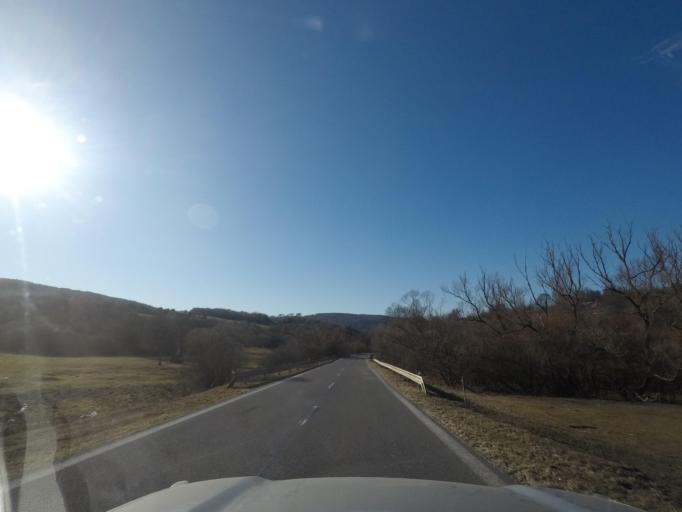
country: PL
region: Subcarpathian Voivodeship
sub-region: Powiat sanocki
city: Komancza
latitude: 49.1606
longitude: 22.0472
